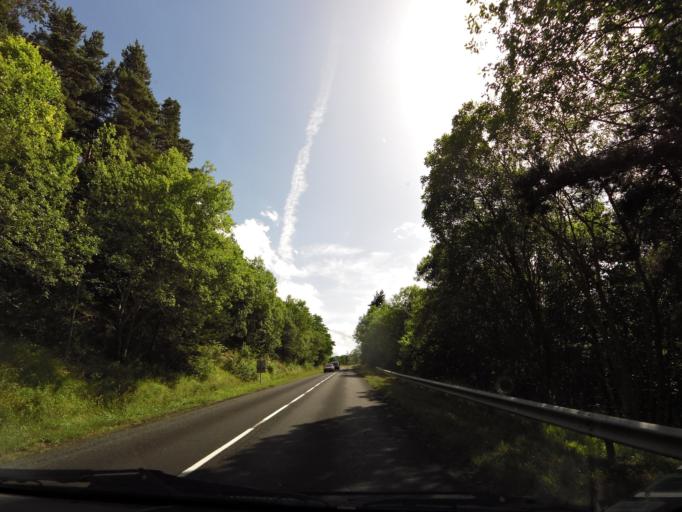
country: FR
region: Auvergne
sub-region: Departement du Puy-de-Dome
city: Aydat
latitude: 45.5667
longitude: 2.9488
